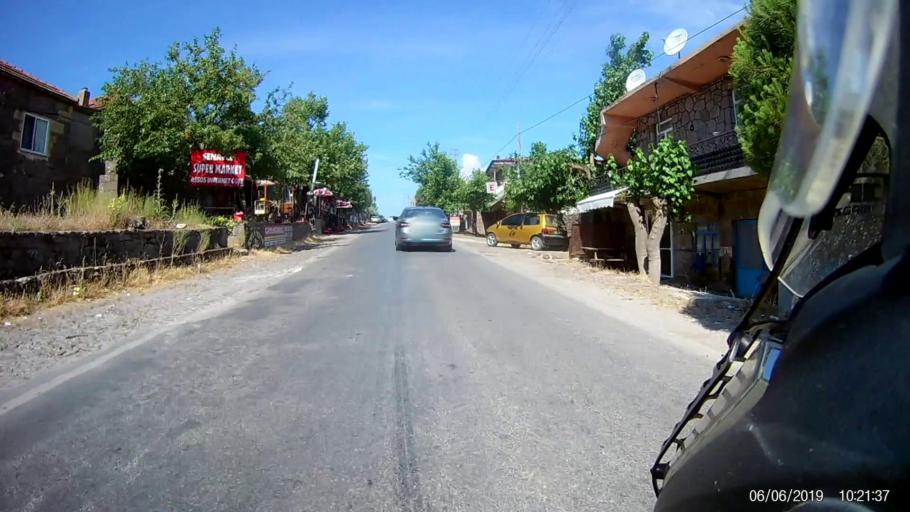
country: TR
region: Canakkale
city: Ayvacik
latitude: 39.5161
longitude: 26.4389
